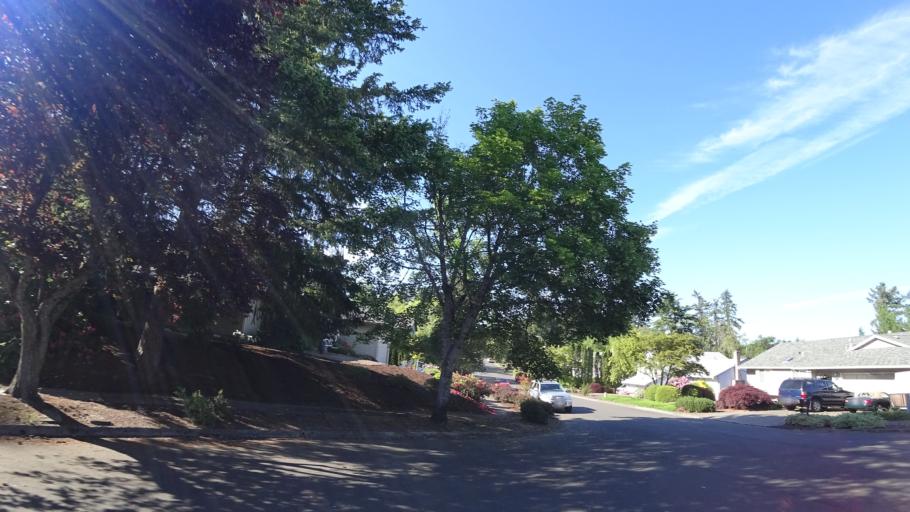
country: US
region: Oregon
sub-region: Washington County
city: Beaverton
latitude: 45.4588
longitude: -122.8065
